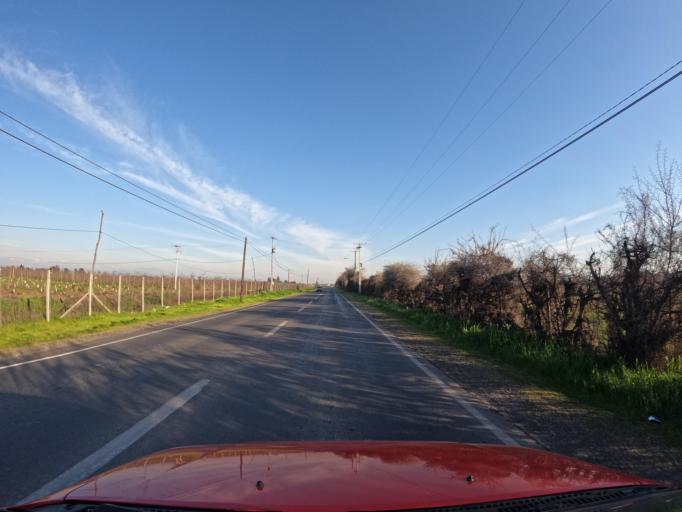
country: CL
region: Maule
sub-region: Provincia de Curico
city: Rauco
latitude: -34.9108
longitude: -71.2782
